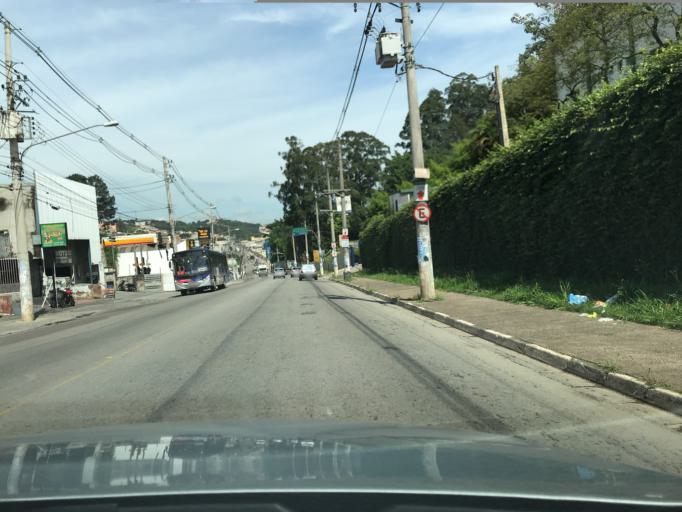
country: BR
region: Sao Paulo
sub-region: Cajamar
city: Cajamar
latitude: -23.4094
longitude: -46.8306
